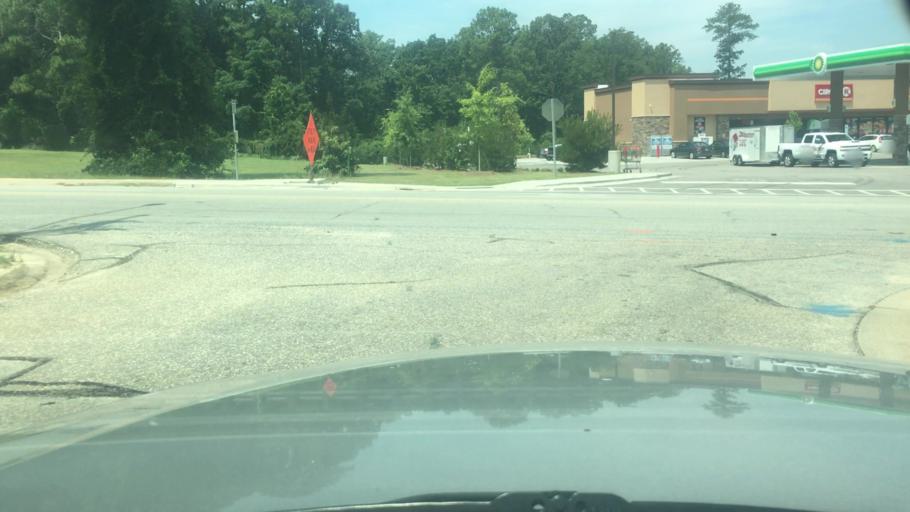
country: US
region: North Carolina
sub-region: Hoke County
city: Rockfish
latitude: 35.0391
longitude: -78.9971
